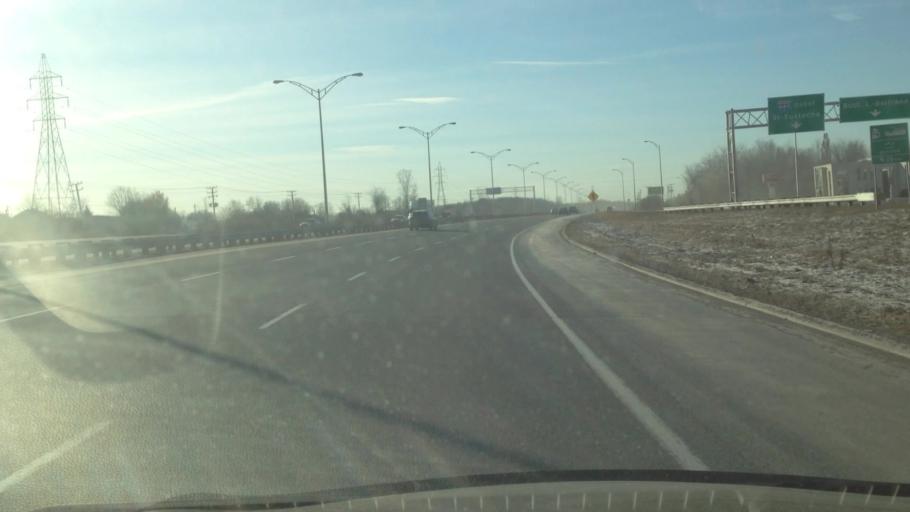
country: CA
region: Quebec
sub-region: Laurentides
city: Boisbriand
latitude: 45.6167
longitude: -73.8507
